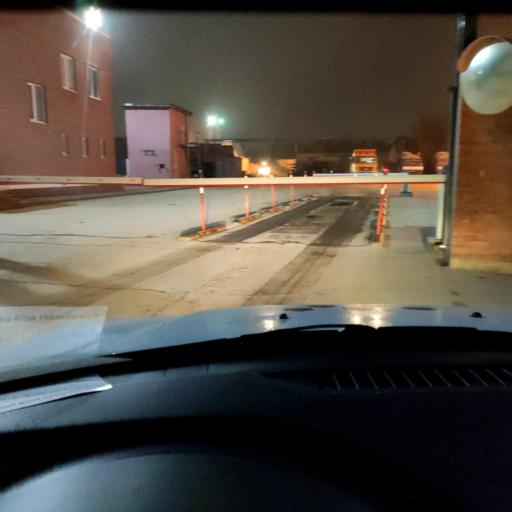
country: RU
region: Samara
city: Zhigulevsk
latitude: 53.5231
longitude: 49.4800
